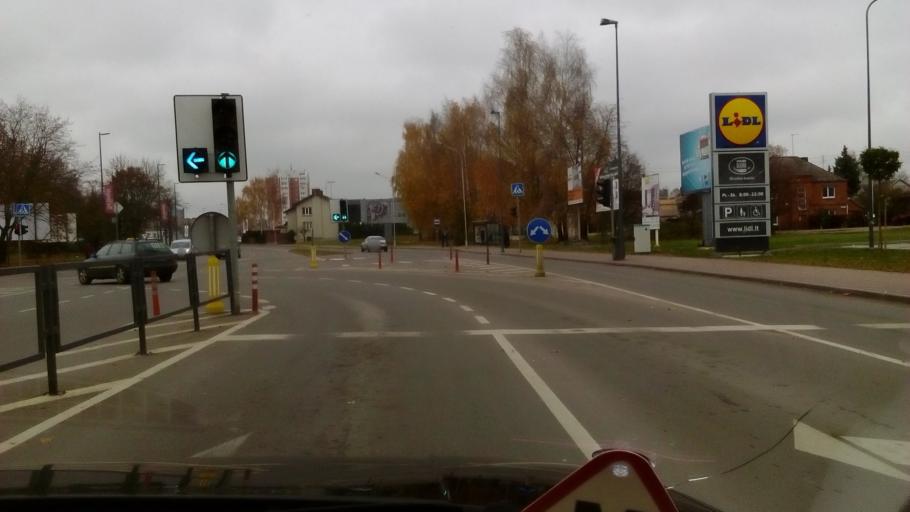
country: LT
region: Marijampoles apskritis
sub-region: Marijampole Municipality
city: Marijampole
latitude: 54.5571
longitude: 23.3546
